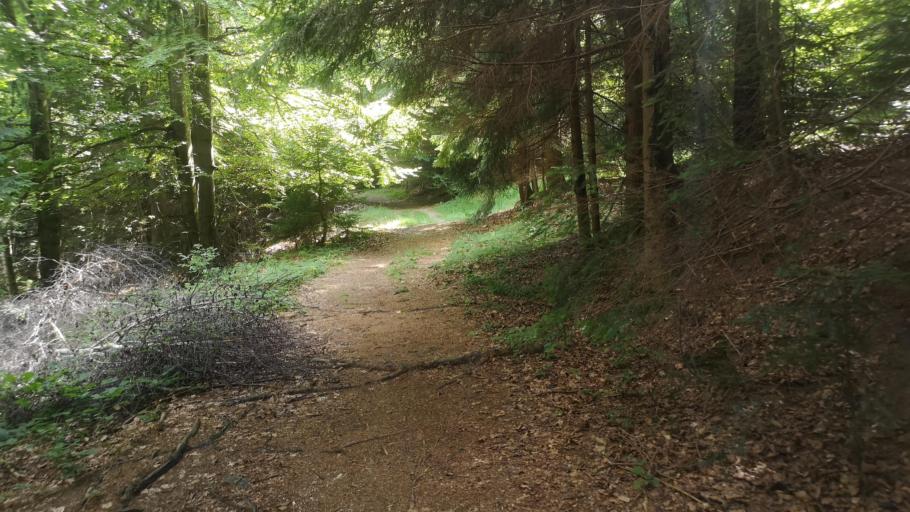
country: SK
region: Zilinsky
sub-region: Okres Zilina
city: Vrutky
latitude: 49.0988
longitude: 18.8536
